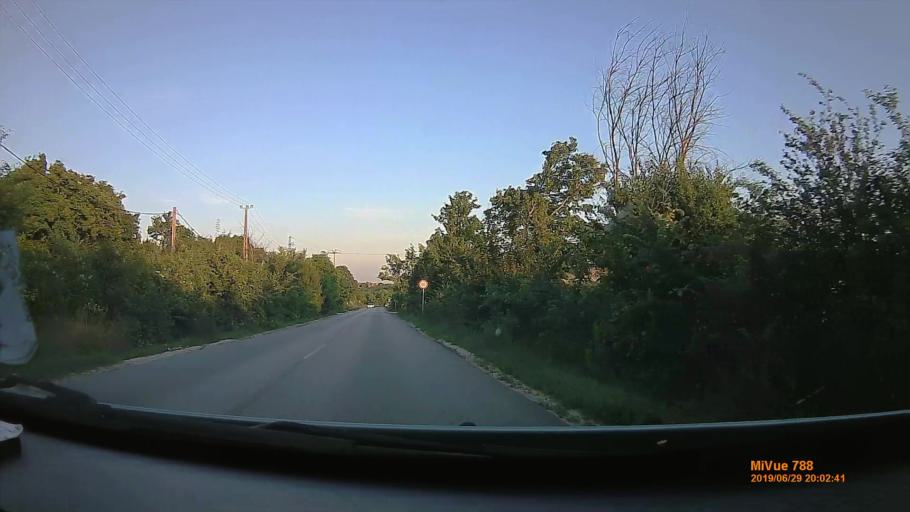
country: HU
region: Pest
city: Zsambek
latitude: 47.5553
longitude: 18.7022
